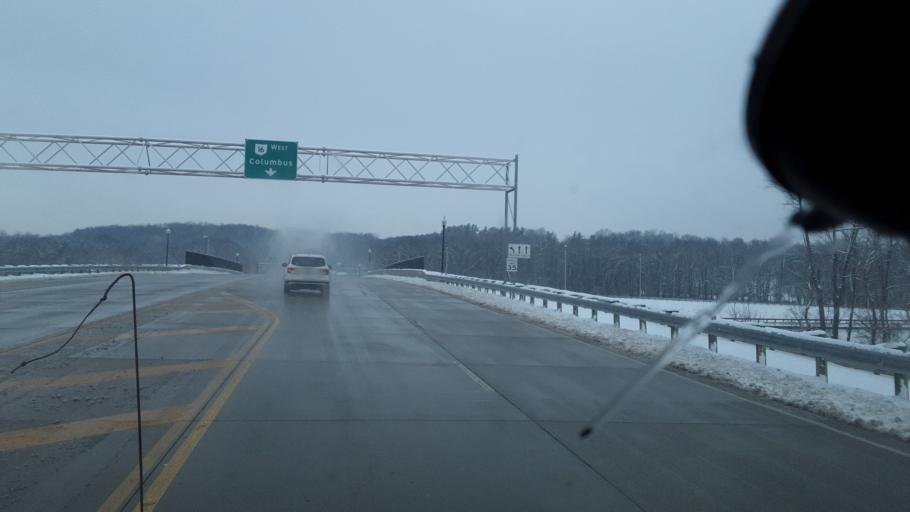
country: US
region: Ohio
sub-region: Licking County
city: Heath
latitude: 40.0523
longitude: -82.4742
